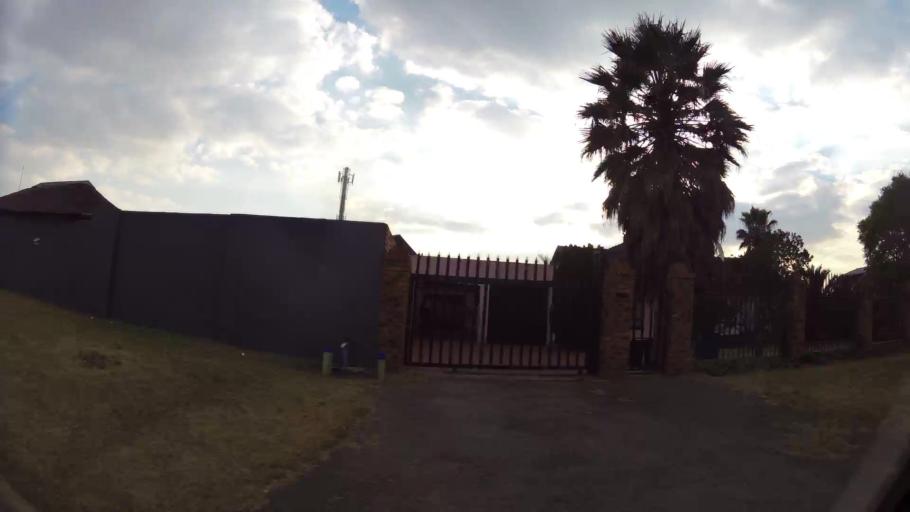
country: ZA
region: Gauteng
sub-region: Ekurhuleni Metropolitan Municipality
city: Germiston
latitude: -26.2379
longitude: 28.1969
